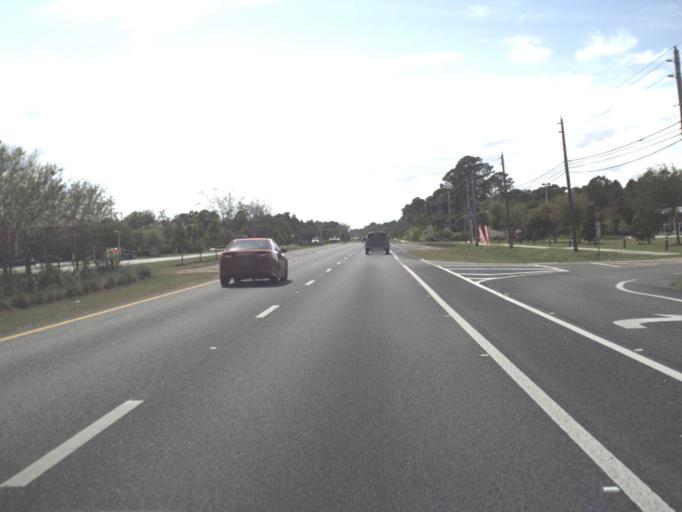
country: US
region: Florida
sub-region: Flagler County
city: Flagler Beach
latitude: 29.4767
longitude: -81.1476
